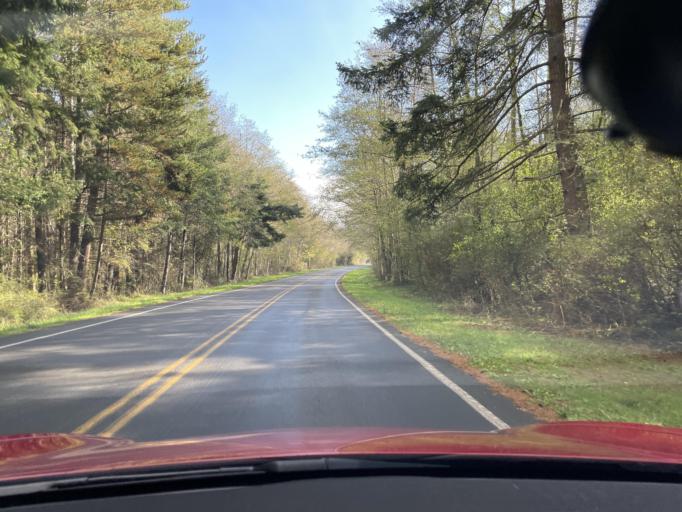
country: US
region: Washington
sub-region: San Juan County
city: Friday Harbor
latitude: 48.4692
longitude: -123.0164
